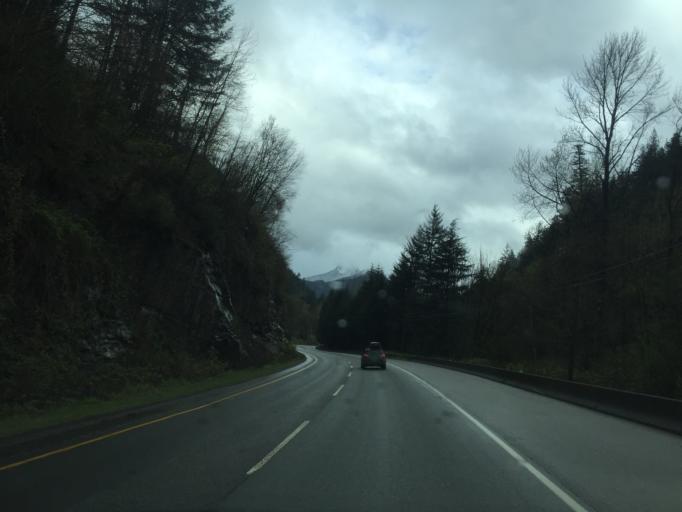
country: CA
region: British Columbia
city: Agassiz
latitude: 49.2653
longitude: -121.6765
